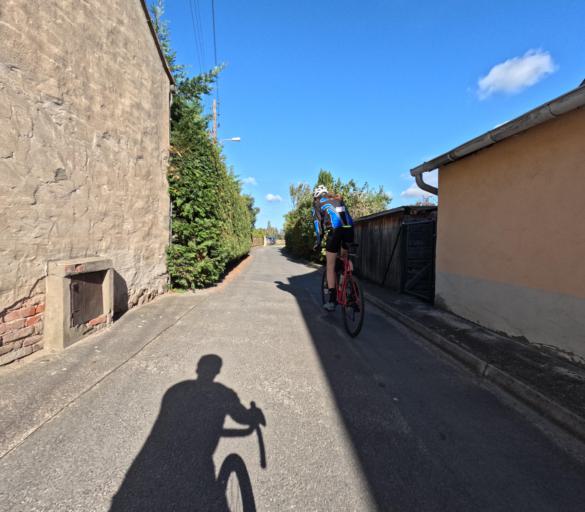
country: DE
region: Saxony
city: Moritzburg
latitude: 51.1406
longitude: 13.6603
